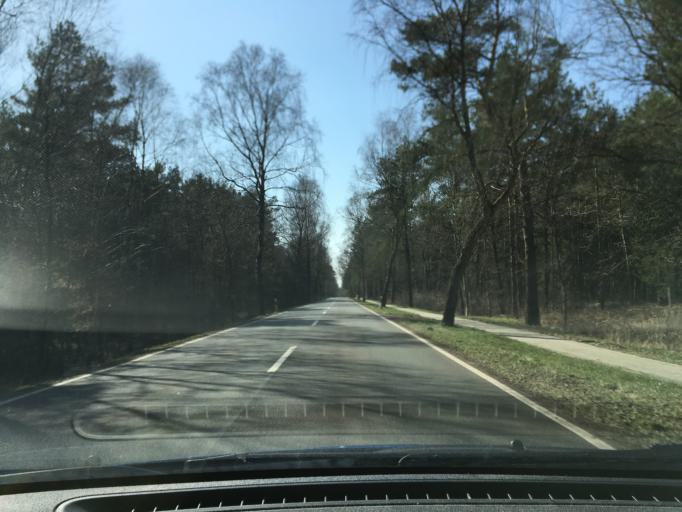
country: DE
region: Lower Saxony
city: Unterluss
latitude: 52.8290
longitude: 10.2389
